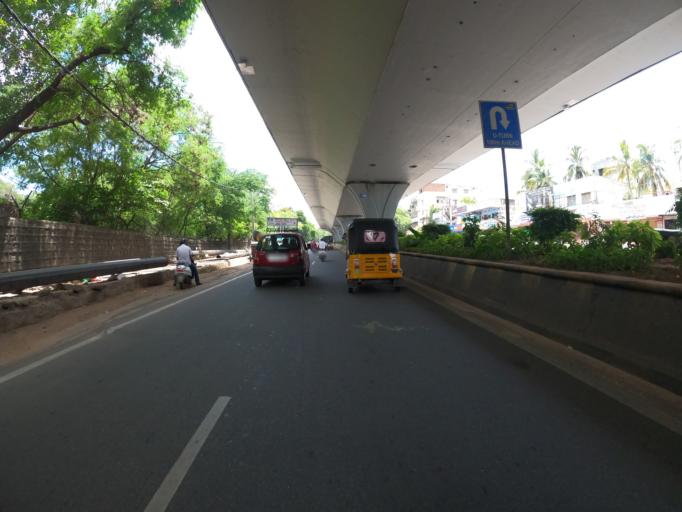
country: IN
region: Telangana
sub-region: Hyderabad
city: Hyderabad
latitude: 17.3853
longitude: 78.4295
